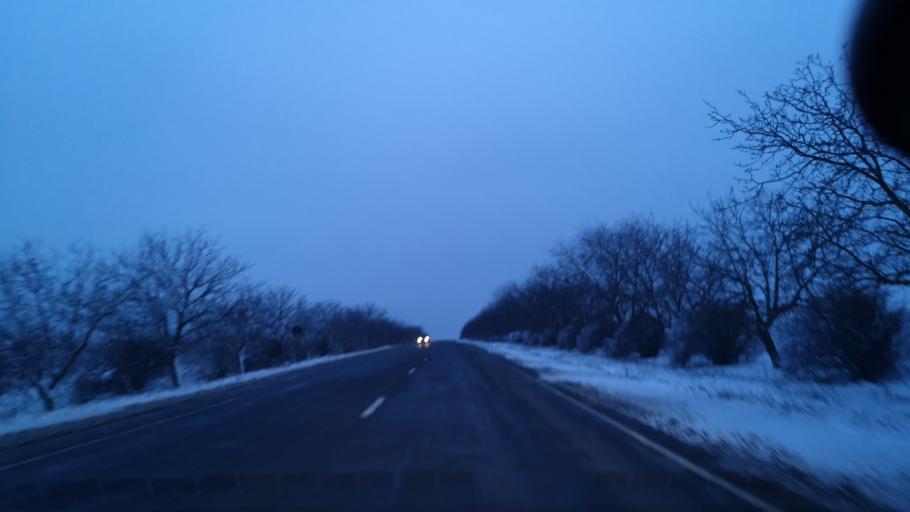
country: MD
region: Rezina
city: Rezina
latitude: 47.7459
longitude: 28.9137
